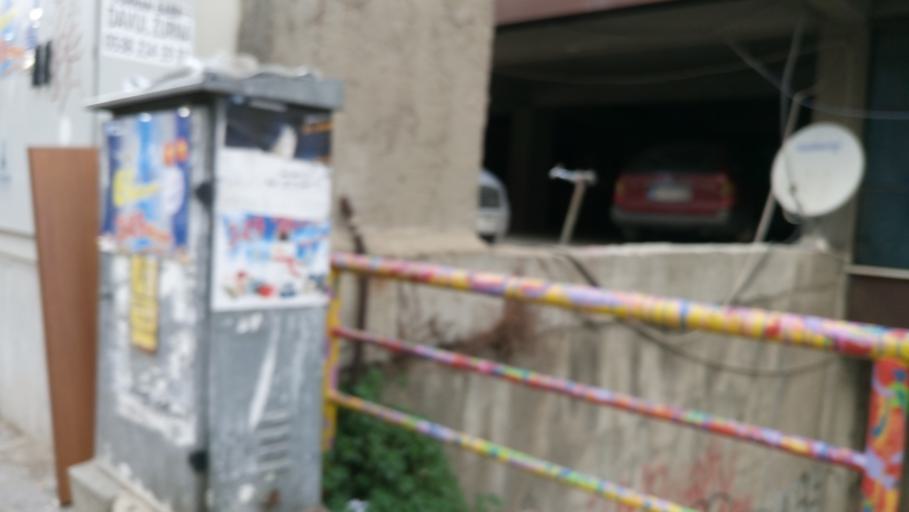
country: TR
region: Izmir
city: Izmir
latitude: 38.4067
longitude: 27.1037
